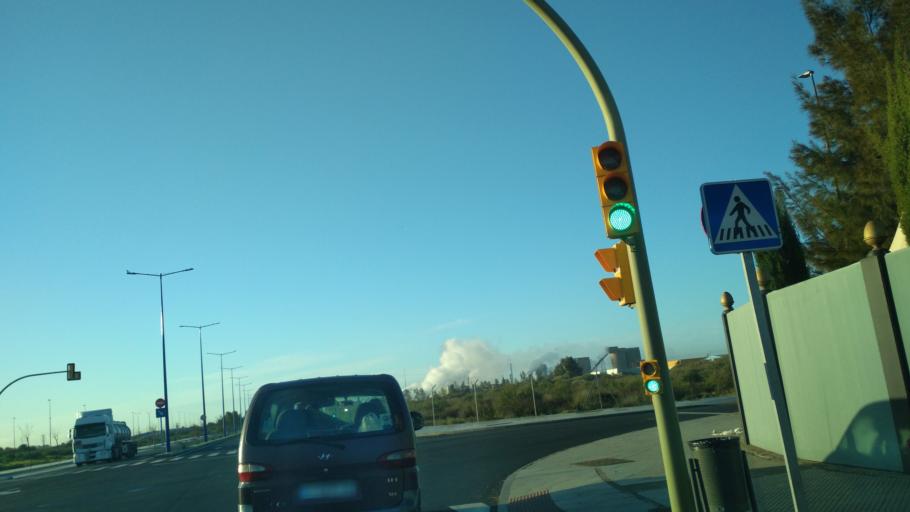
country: ES
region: Andalusia
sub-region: Provincia de Huelva
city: Huelva
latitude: 37.2421
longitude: -6.9458
